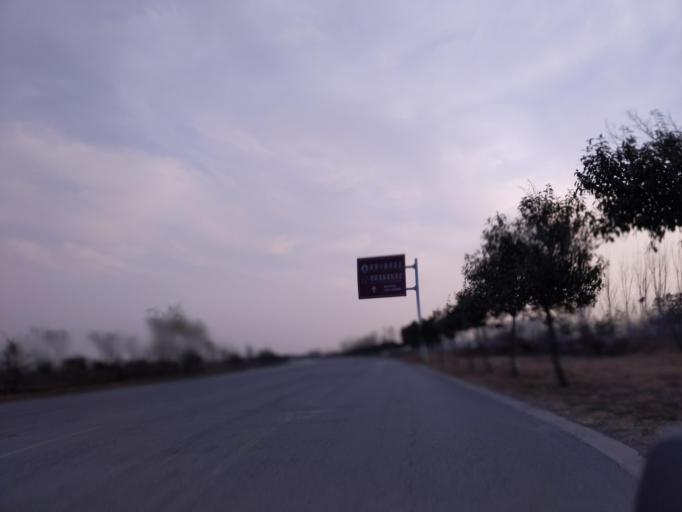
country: CN
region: Henan Sheng
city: Puyang
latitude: 35.8152
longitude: 114.9679
